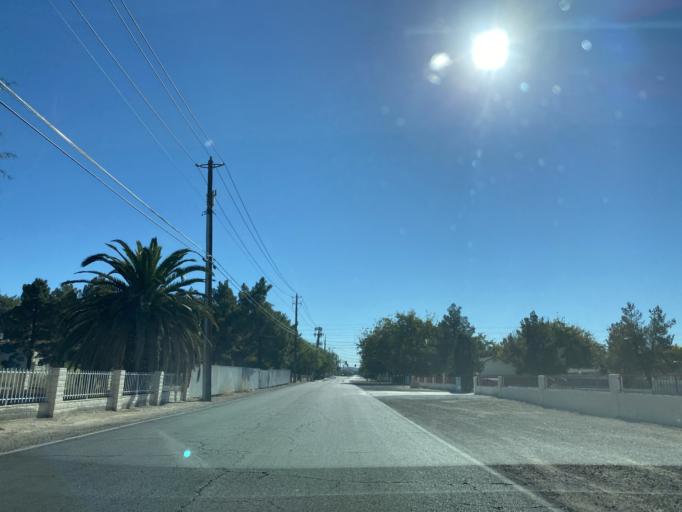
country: US
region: Nevada
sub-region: Clark County
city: Whitney
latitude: 36.0878
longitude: -115.0868
